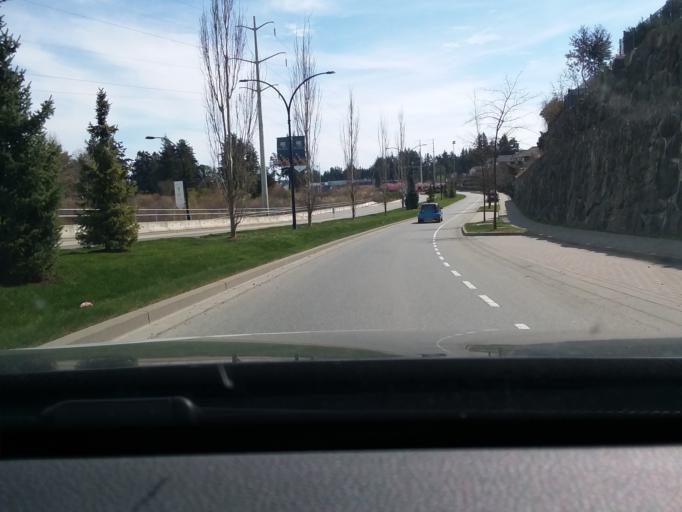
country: CA
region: British Columbia
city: Langford
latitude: 48.4451
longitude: -123.5314
